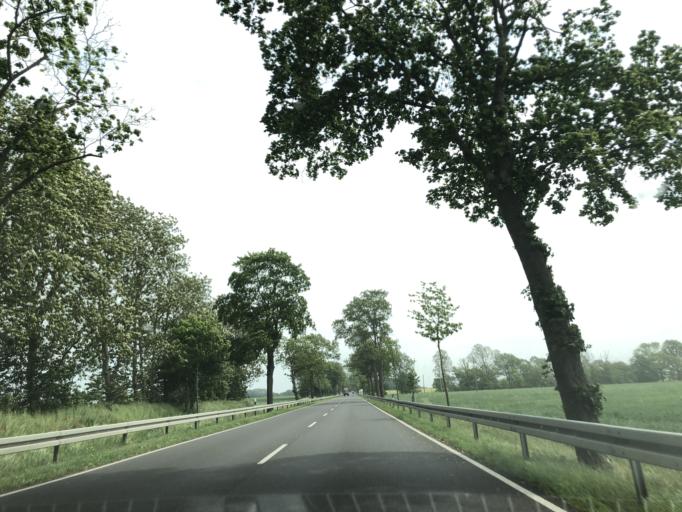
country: DE
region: Brandenburg
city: Gumtow
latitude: 52.9665
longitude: 12.3214
